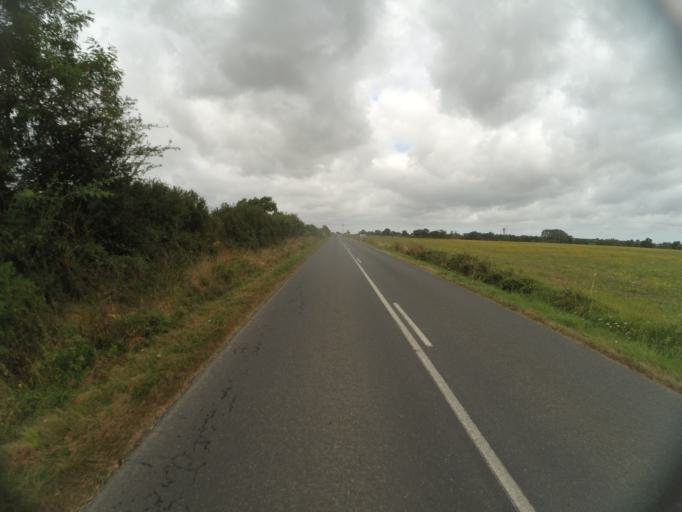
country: FR
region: Pays de la Loire
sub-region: Departement de Maine-et-Loire
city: Saint-Crespin-sur-Moine
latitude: 47.0814
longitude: -1.1693
